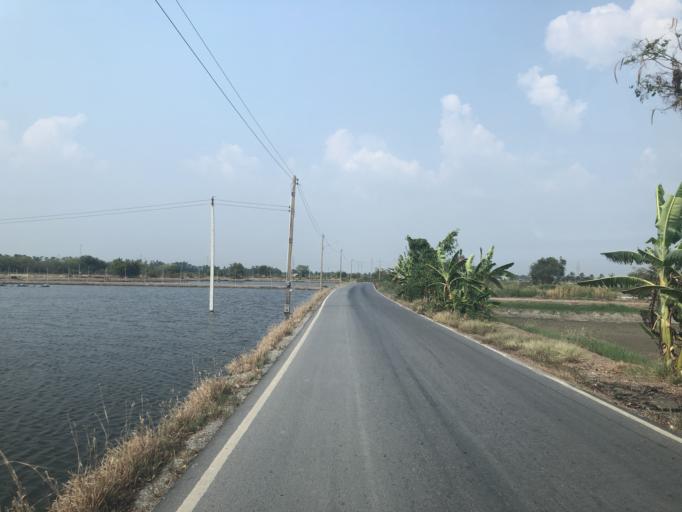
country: TH
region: Chachoengsao
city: Bang Pakong
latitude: 13.5148
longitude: 100.9239
